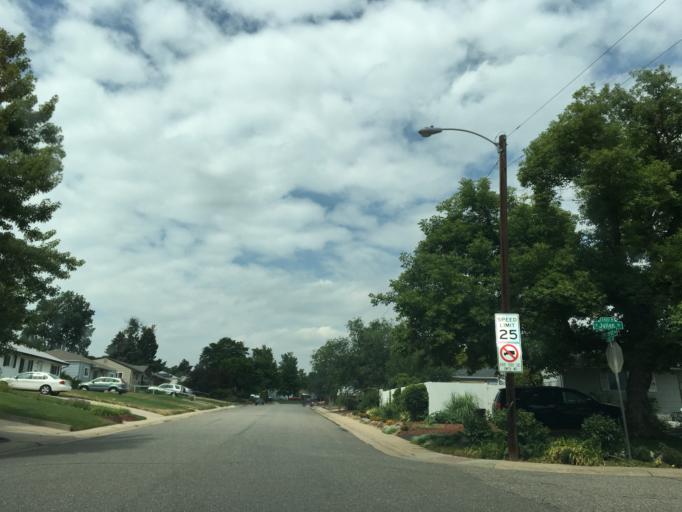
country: US
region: Colorado
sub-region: Arapahoe County
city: Sheridan
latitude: 39.6650
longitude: -105.0308
